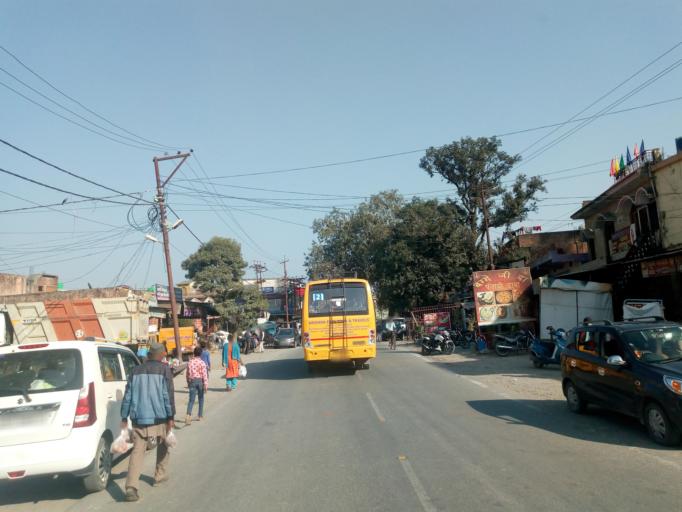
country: IN
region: Uttarakhand
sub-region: Dehradun
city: Harbatpur
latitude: 30.4409
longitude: 77.7321
